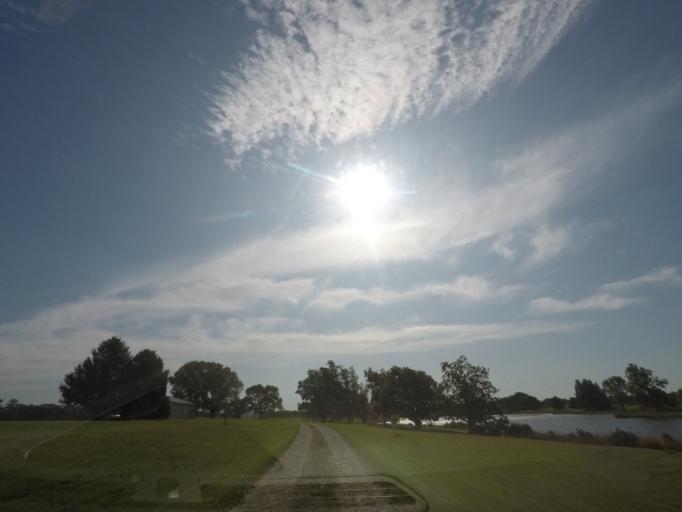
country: US
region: Iowa
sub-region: Story County
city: Gilbert
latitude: 42.1129
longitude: -93.5844
